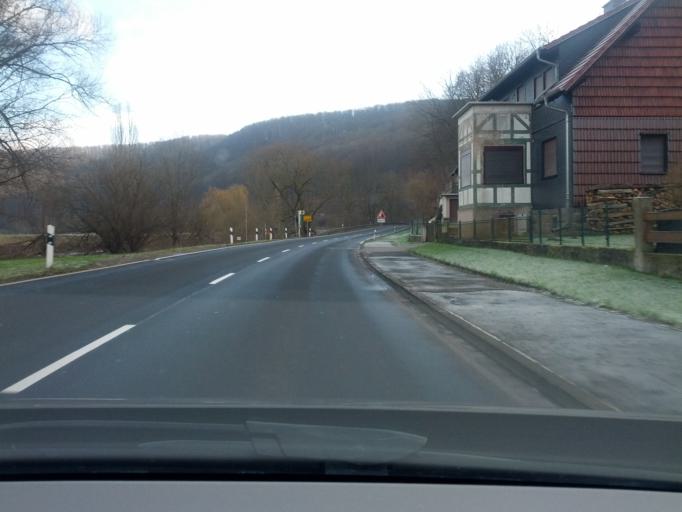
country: DE
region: Hesse
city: Witzenhausen
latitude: 51.3185
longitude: 9.8873
